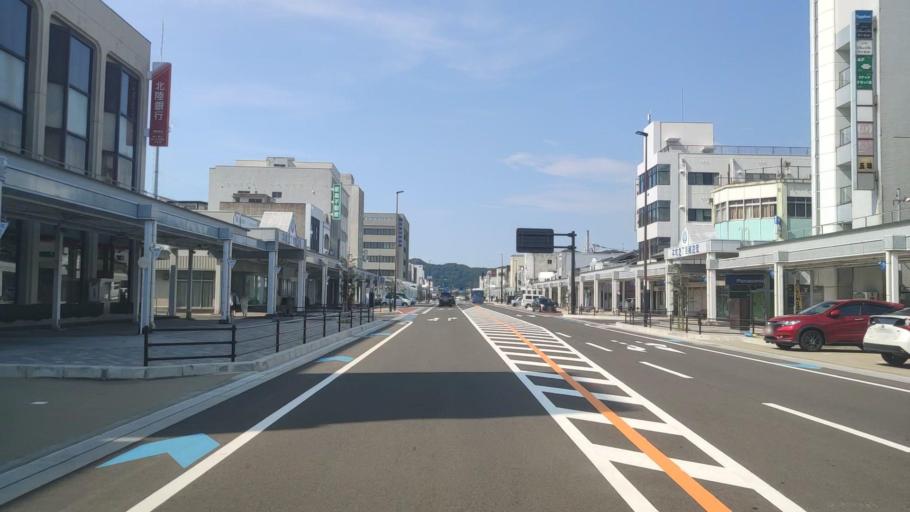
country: JP
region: Fukui
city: Tsuruga
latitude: 35.6498
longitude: 136.0724
